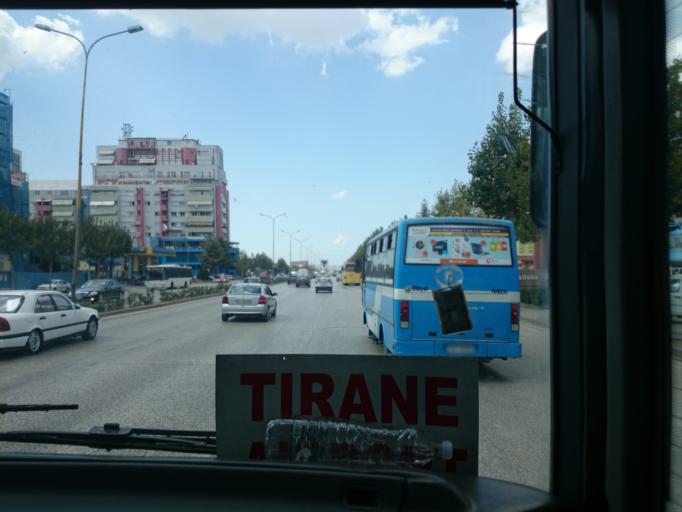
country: AL
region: Tirane
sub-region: Rrethi i Tiranes
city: Paskuqan
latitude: 41.3379
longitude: 19.7904
